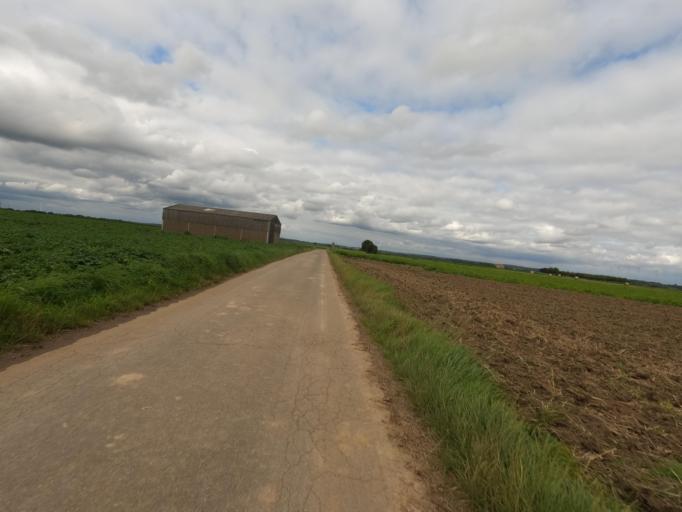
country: DE
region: North Rhine-Westphalia
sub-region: Regierungsbezirk Koln
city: Linnich
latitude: 50.9913
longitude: 6.2389
